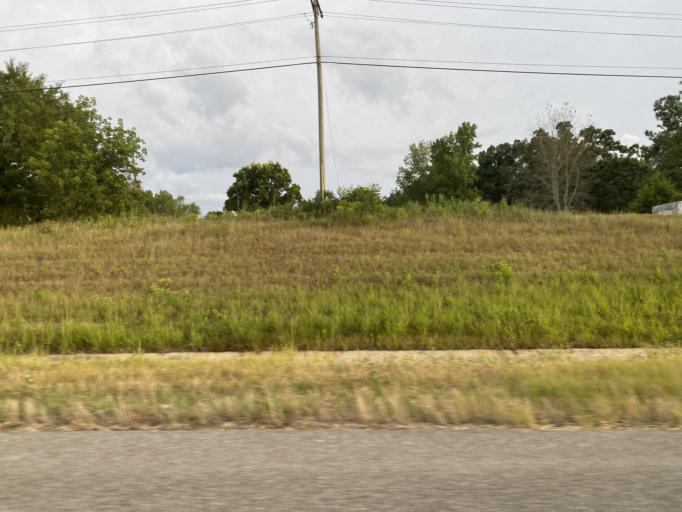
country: US
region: Alabama
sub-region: Franklin County
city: Red Bay
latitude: 34.4492
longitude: -88.0678
